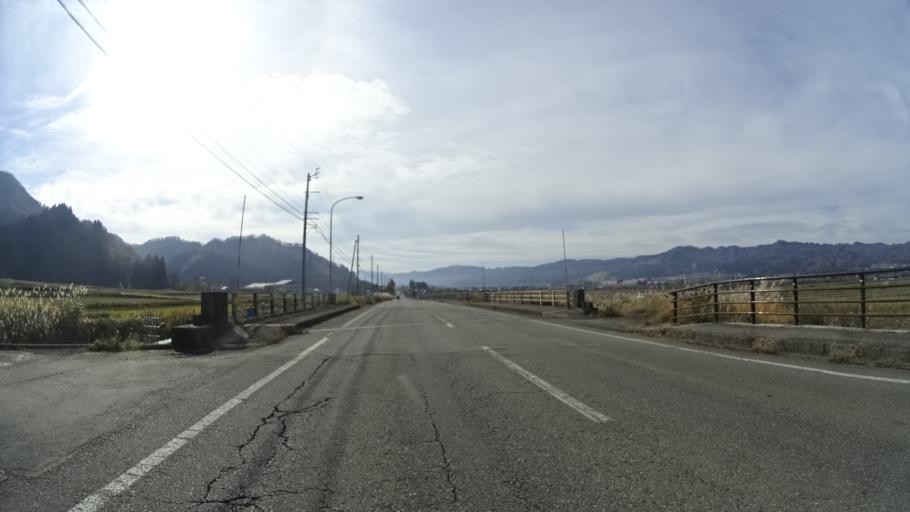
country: JP
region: Niigata
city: Muikamachi
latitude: 37.1280
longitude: 138.9361
